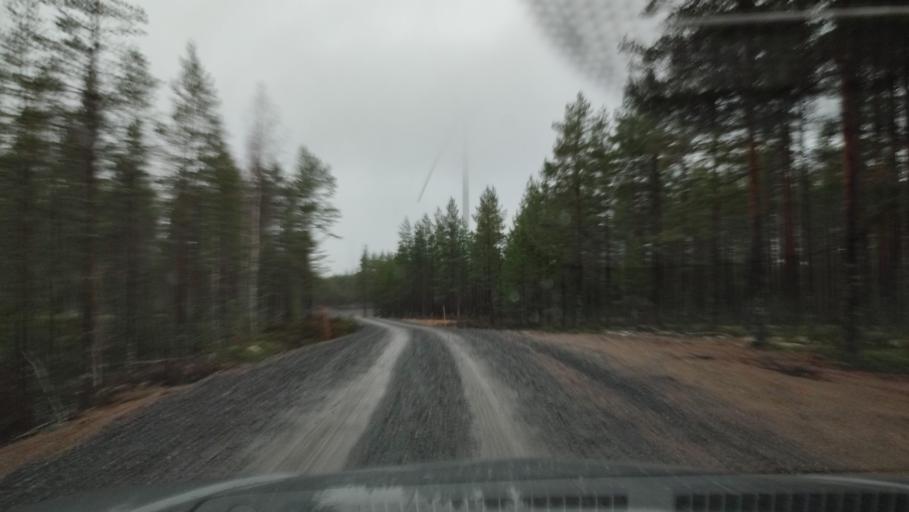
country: FI
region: Southern Ostrobothnia
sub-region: Suupohja
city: Karijoki
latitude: 62.1568
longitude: 21.6160
